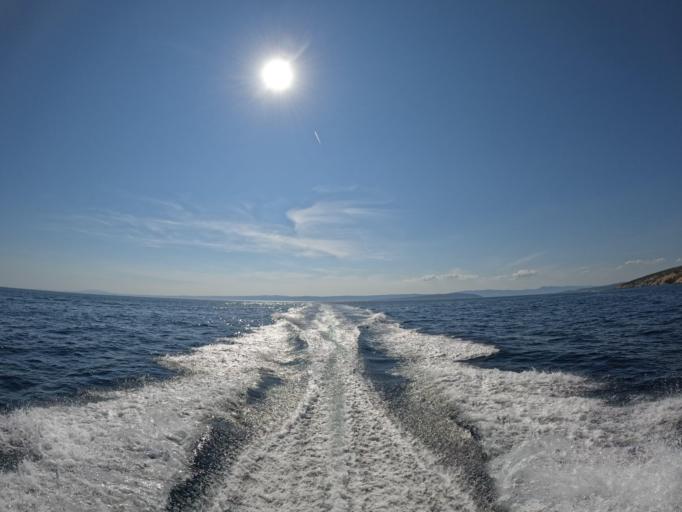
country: HR
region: Primorsko-Goranska
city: Punat
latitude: 44.9610
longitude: 14.6496
